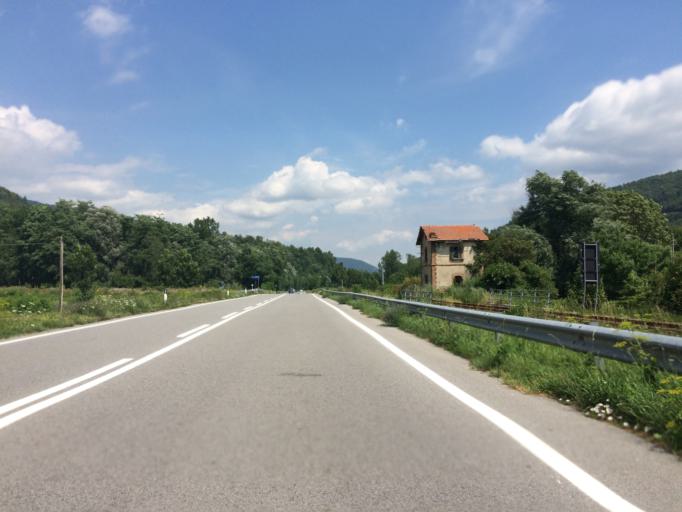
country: IT
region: Piedmont
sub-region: Provincia di Cuneo
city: Garessio
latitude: 44.2214
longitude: 8.0150
